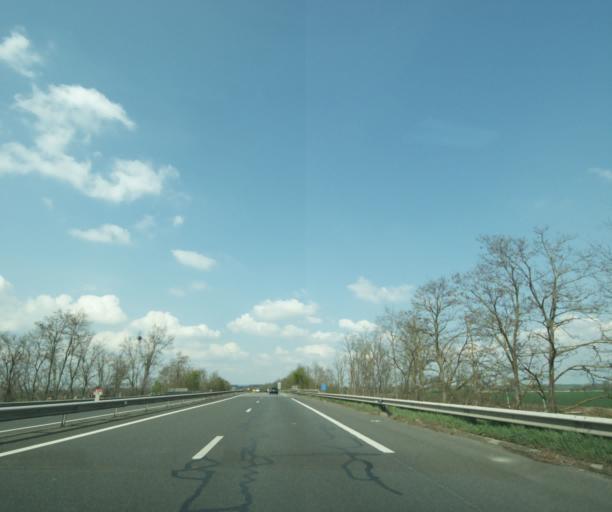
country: FR
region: Auvergne
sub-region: Departement du Puy-de-Dome
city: Riom
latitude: 45.9020
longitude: 3.1545
